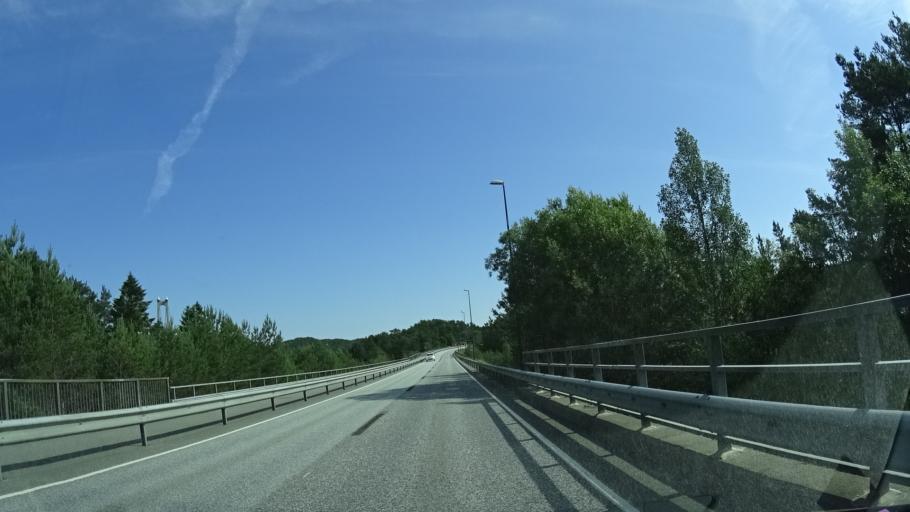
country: NO
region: Hordaland
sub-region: Bomlo
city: Mosterhamn
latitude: 59.7384
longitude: 5.3978
